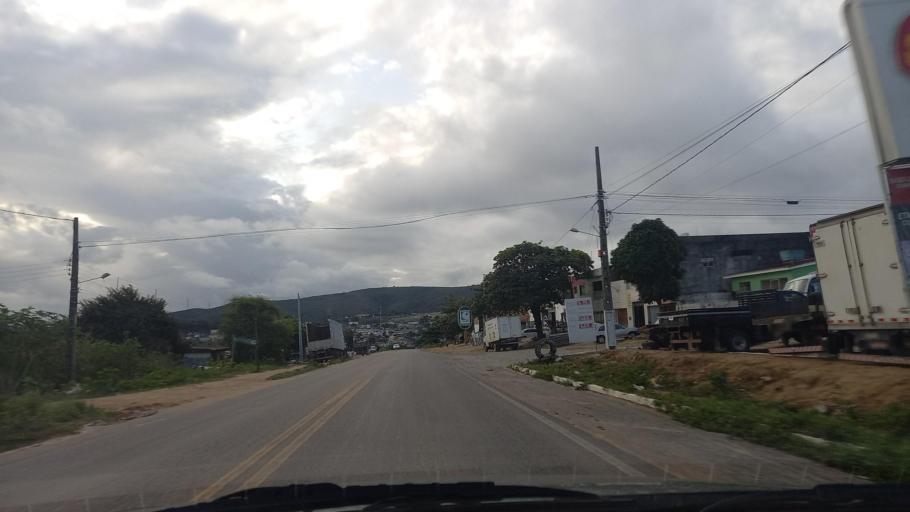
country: BR
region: Pernambuco
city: Garanhuns
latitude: -8.9024
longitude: -36.5009
